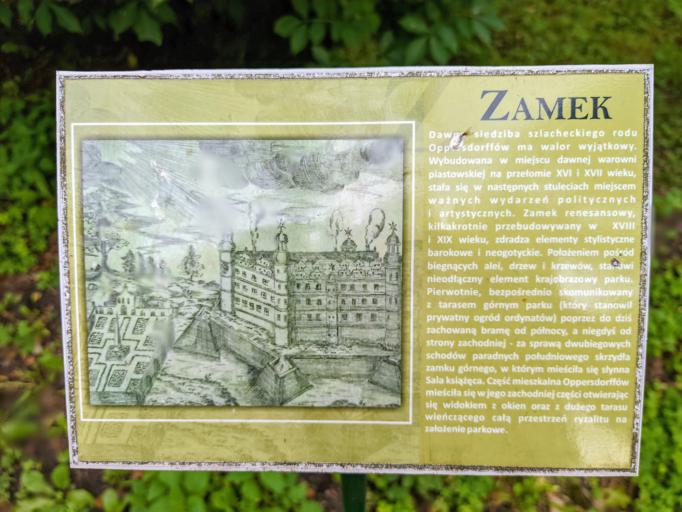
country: PL
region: Opole Voivodeship
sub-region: Powiat prudnicki
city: Glogowek
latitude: 50.3562
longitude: 17.8615
